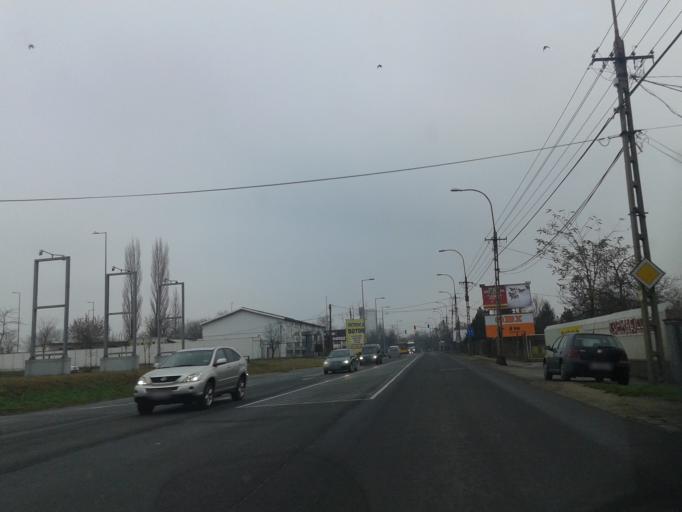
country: HU
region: Budapest
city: Budapest XXII. keruelet
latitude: 47.4018
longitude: 19.0520
